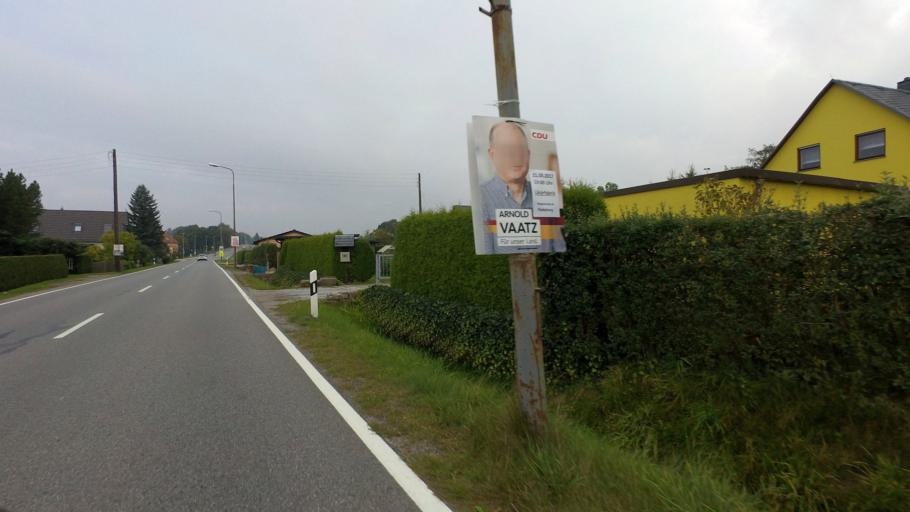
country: DE
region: Saxony
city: Arnsdorf
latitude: 51.0887
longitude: 14.0120
